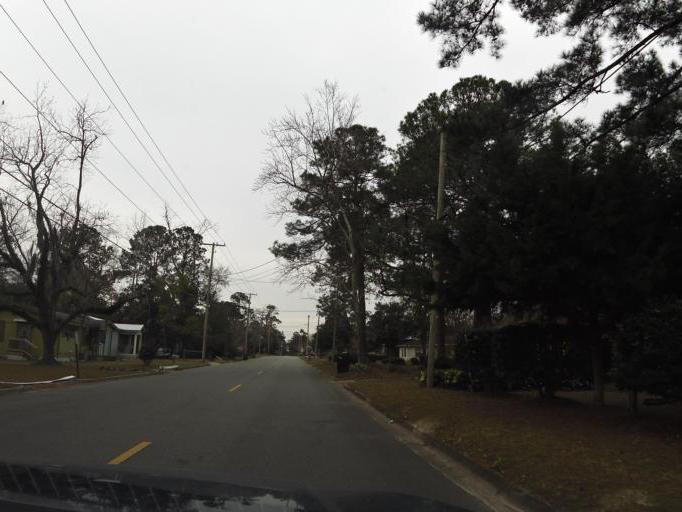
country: US
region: Georgia
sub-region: Thomas County
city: Thomasville
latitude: 30.8159
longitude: -83.9797
